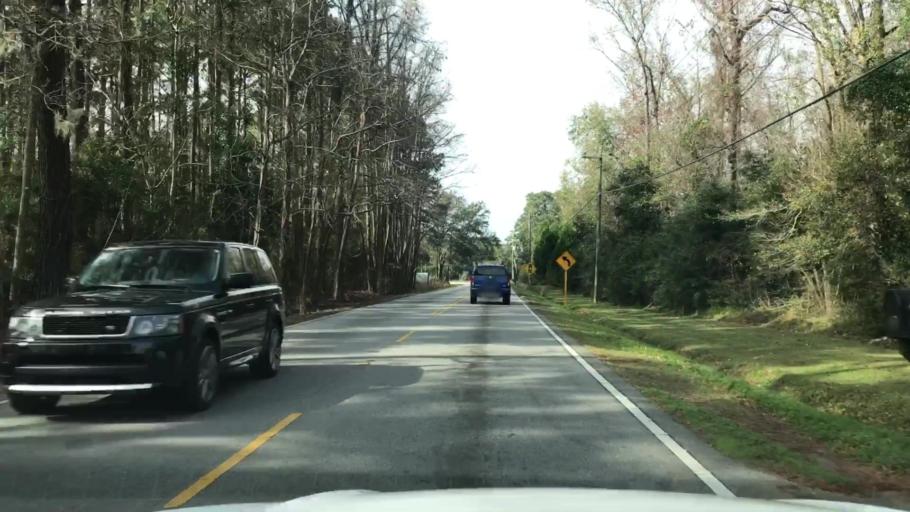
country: US
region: South Carolina
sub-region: Charleston County
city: Shell Point
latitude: 32.7790
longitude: -80.1019
